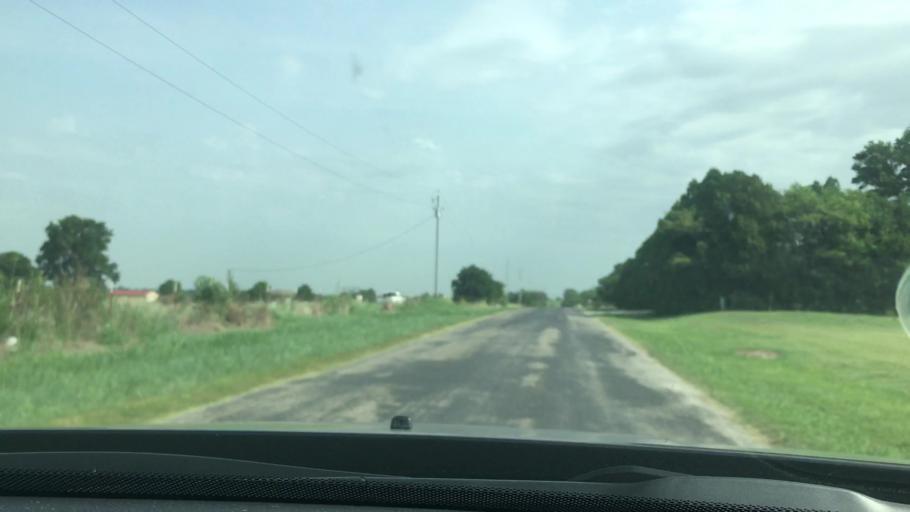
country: US
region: Oklahoma
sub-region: Garvin County
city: Pauls Valley
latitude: 34.8124
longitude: -97.1956
